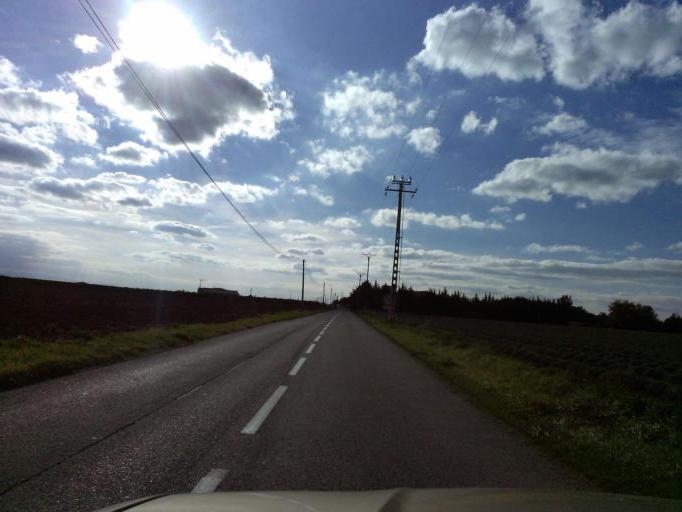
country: FR
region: Provence-Alpes-Cote d'Azur
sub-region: Departement des Alpes-de-Haute-Provence
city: Valensole
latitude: 43.8823
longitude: 6.0434
